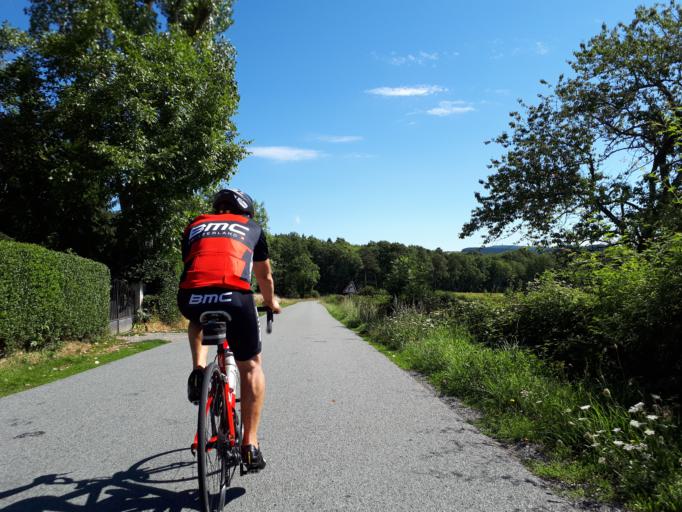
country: FR
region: Rhone-Alpes
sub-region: Departement de la Loire
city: Bussieres
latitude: 45.8301
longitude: 4.2910
